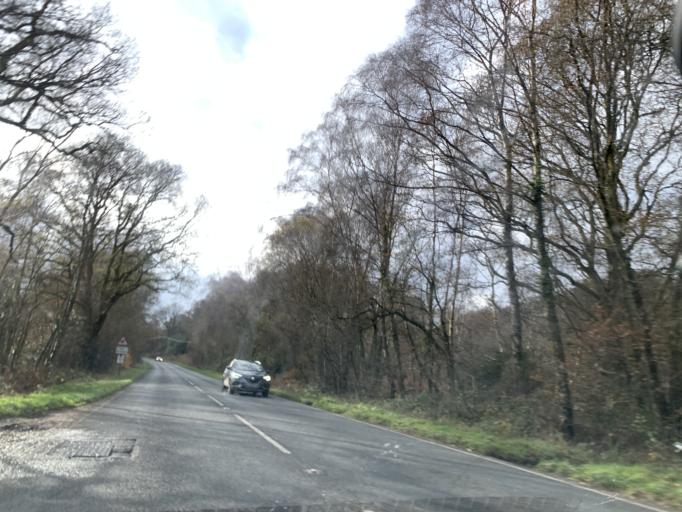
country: GB
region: England
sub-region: Hampshire
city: Lyndhurst
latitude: 50.8612
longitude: -1.6013
